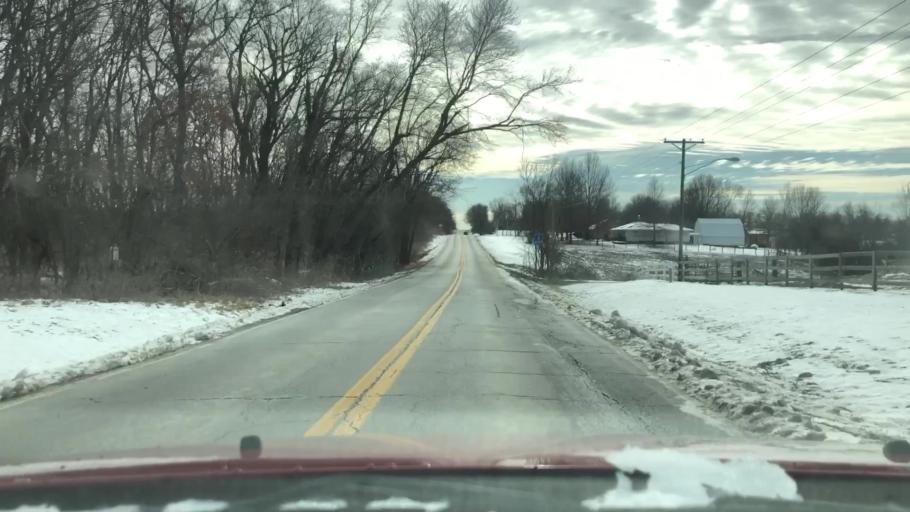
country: US
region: Missouri
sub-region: Jackson County
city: Greenwood
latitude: 38.8796
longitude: -94.3410
